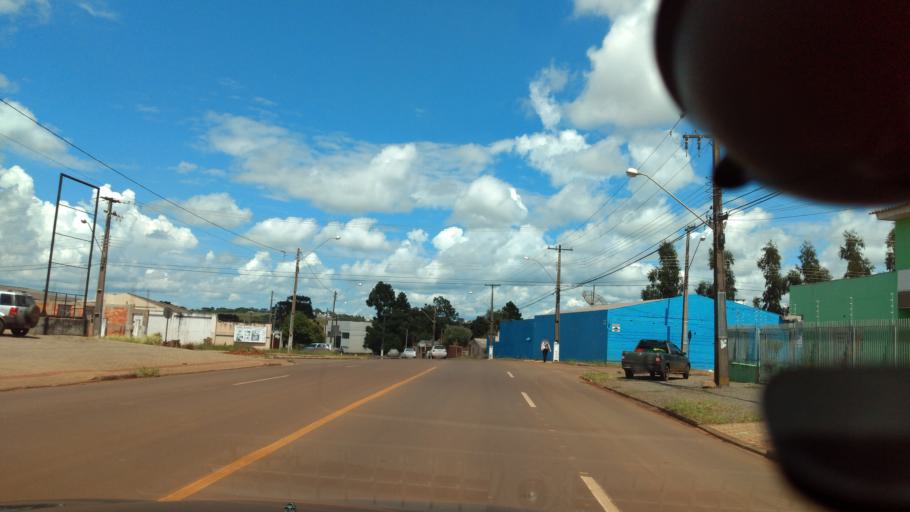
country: BR
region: Parana
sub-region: Guarapuava
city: Guarapuava
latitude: -25.3929
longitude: -51.4974
